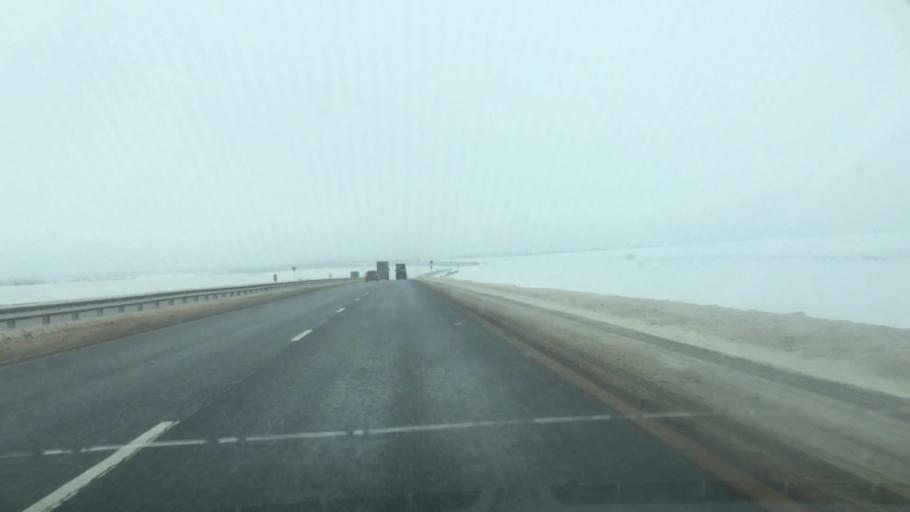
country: RU
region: Lipetsk
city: Stanovoye
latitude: 52.7929
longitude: 38.3439
